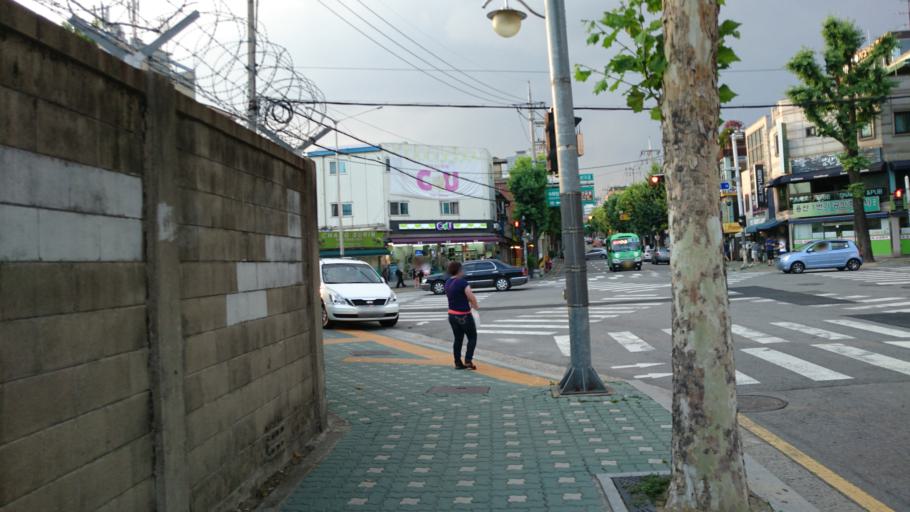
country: KR
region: Seoul
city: Seoul
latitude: 37.5456
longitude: 126.9786
